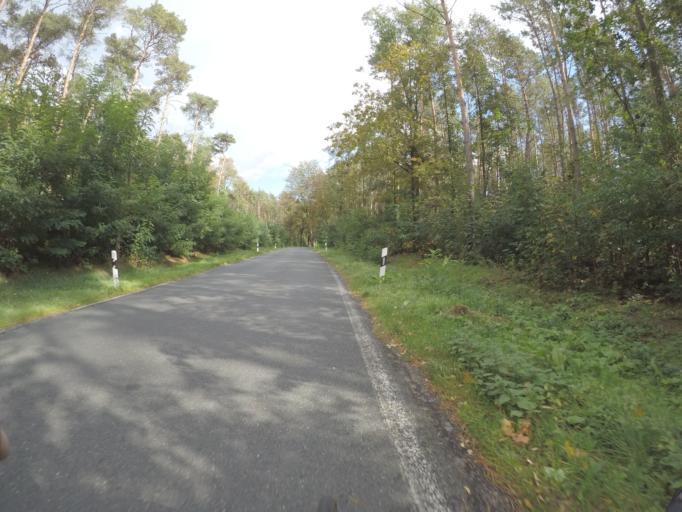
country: DE
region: Brandenburg
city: Strausberg
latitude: 52.6023
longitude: 13.8498
